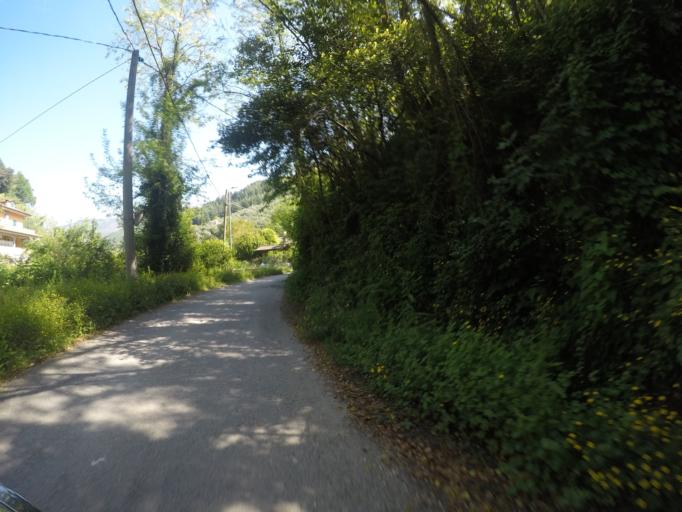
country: IT
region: Tuscany
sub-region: Provincia di Massa-Carrara
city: Massa
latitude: 44.0675
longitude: 10.1090
